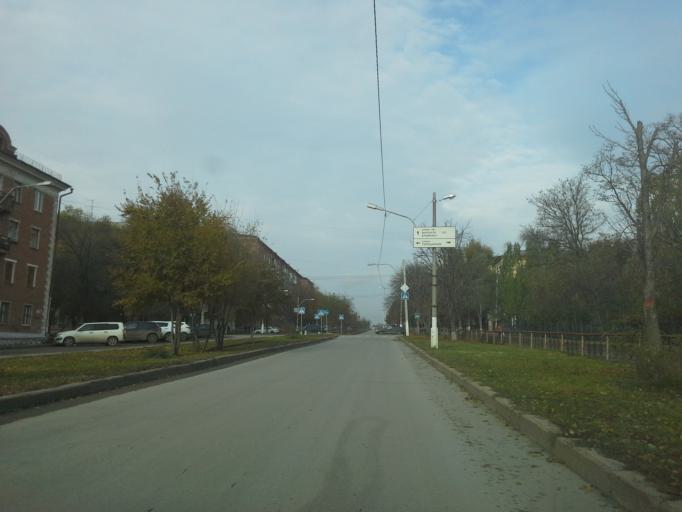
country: RU
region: Volgograd
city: Vodstroy
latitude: 48.7801
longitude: 44.5709
